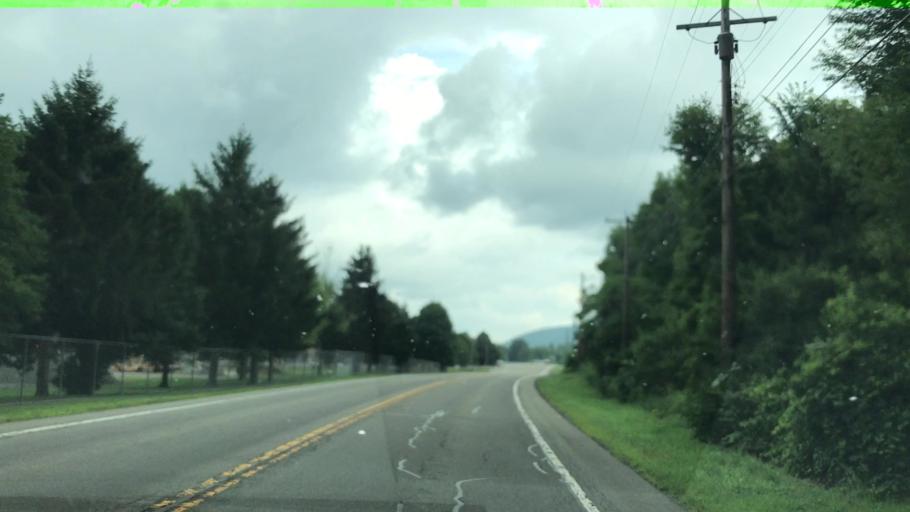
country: US
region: New York
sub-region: Steuben County
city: Bath
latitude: 42.3833
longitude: -77.3594
